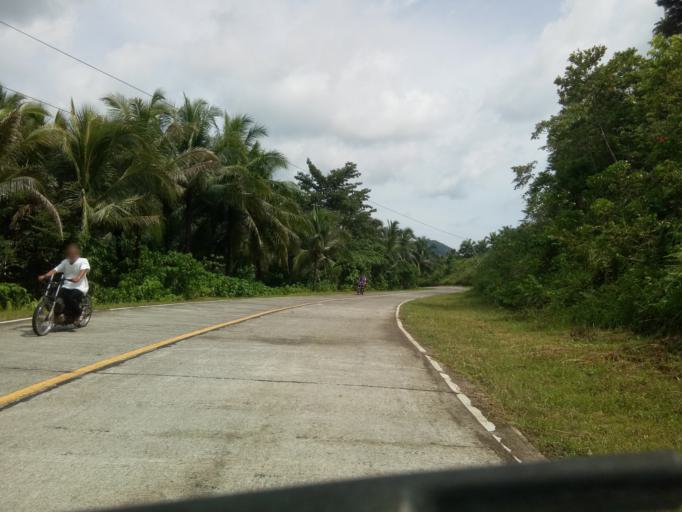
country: PH
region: Caraga
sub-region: Province of Surigao del Norte
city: Pilar
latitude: 9.8617
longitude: 126.0628
